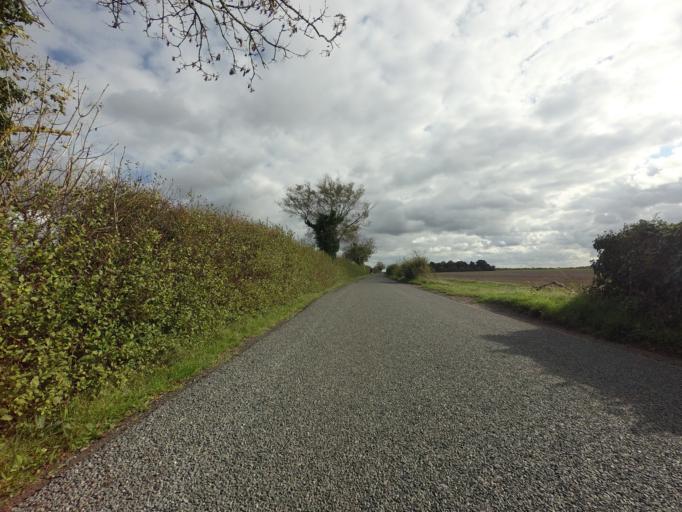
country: GB
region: England
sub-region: Norfolk
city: Dersingham
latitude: 52.8586
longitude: 0.5144
